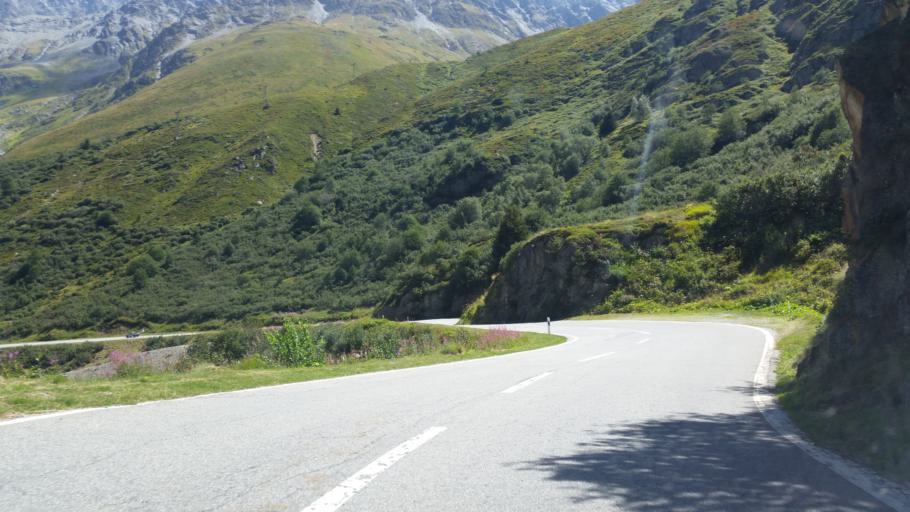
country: IT
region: Aosta Valley
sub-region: Valle d'Aosta
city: San Leonardo
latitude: 45.8988
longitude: 7.1912
